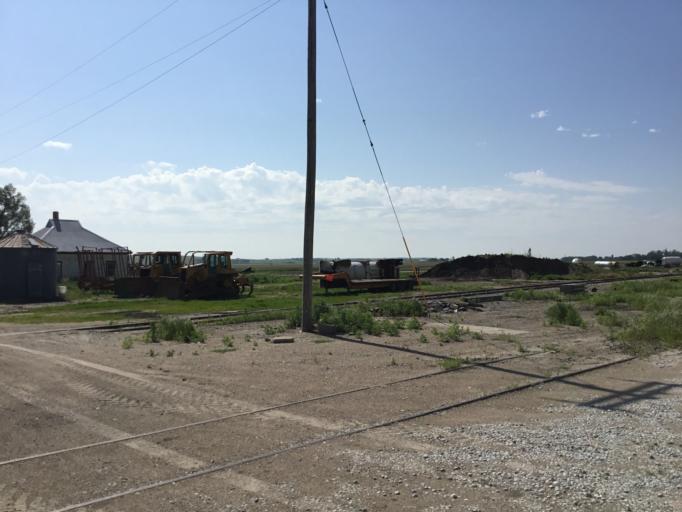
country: US
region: Kansas
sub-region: Cloud County
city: Concordia
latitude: 39.6963
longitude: -97.7741
